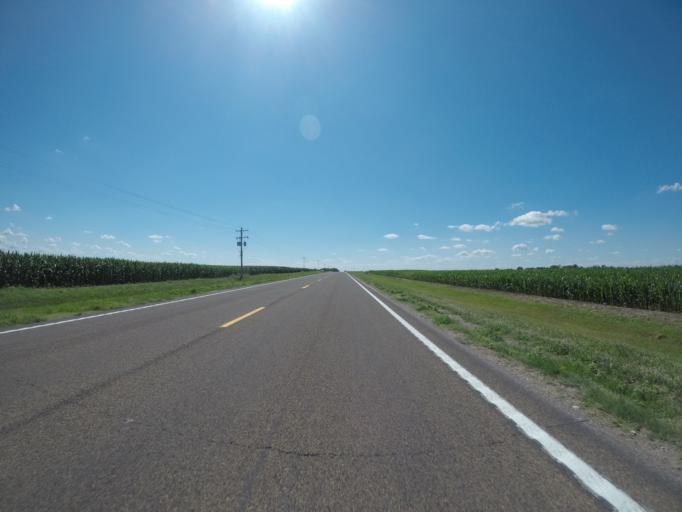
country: US
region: Nebraska
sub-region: Chase County
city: Imperial
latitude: 40.5377
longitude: -101.7172
